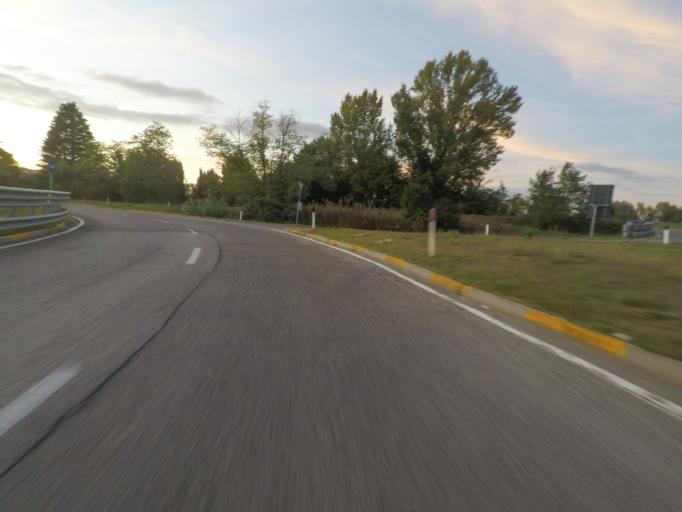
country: IT
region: Tuscany
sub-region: Provincia di Siena
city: Sinalunga
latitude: 43.2217
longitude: 11.7571
